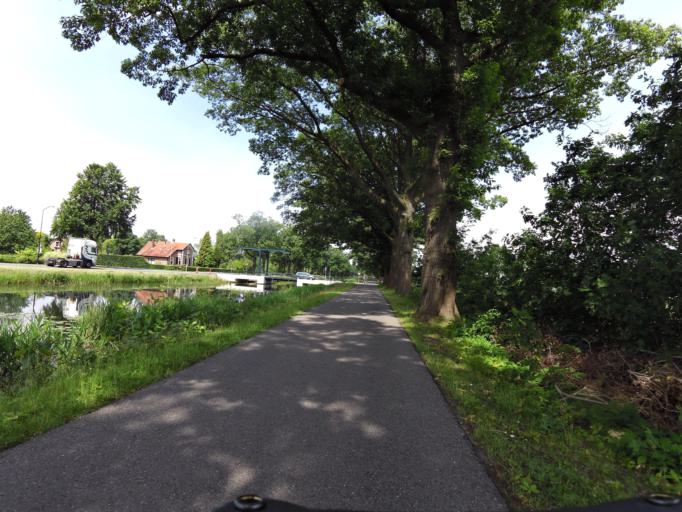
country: NL
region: Gelderland
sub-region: Gemeente Apeldoorn
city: Loenen
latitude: 52.1332
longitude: 6.0436
